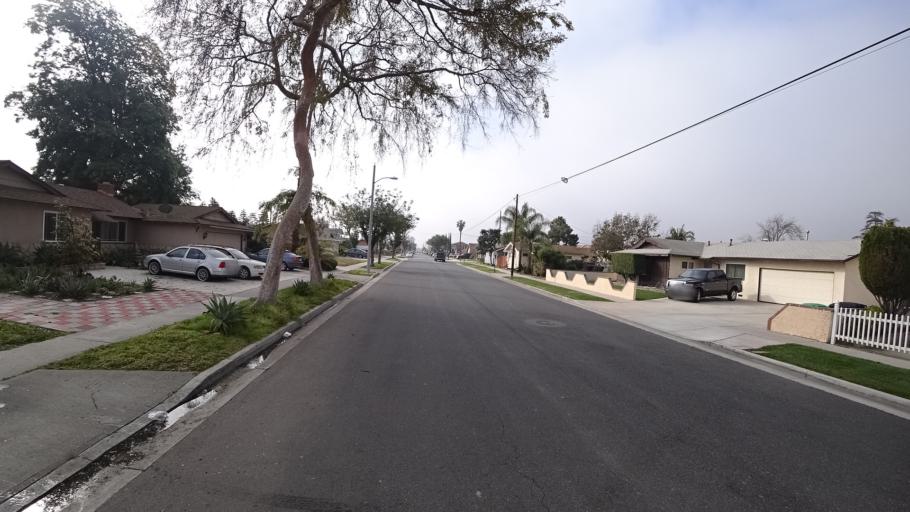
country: US
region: California
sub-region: Orange County
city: Stanton
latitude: 33.8155
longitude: -117.9889
